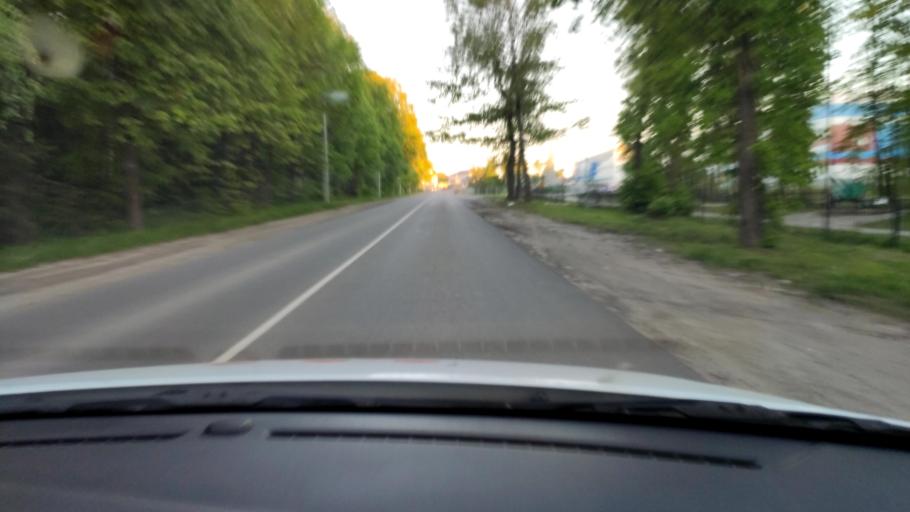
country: RU
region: Tatarstan
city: Vysokaya Gora
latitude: 55.9253
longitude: 49.3036
